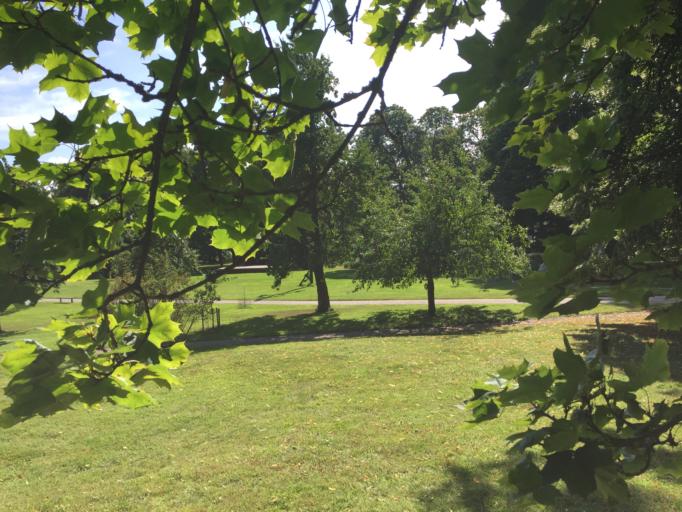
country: SE
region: Soedermanland
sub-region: Vingakers Kommun
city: Vingaker
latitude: 59.1506
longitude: 16.0395
